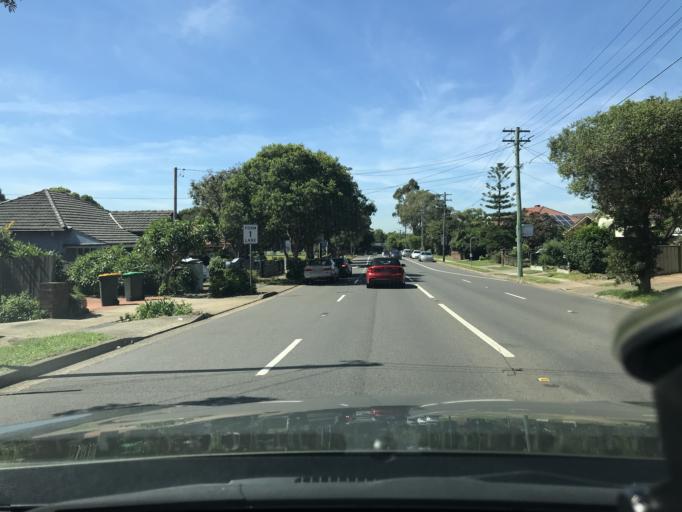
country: AU
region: New South Wales
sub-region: Canada Bay
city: Concord
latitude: -33.8659
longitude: 151.1064
